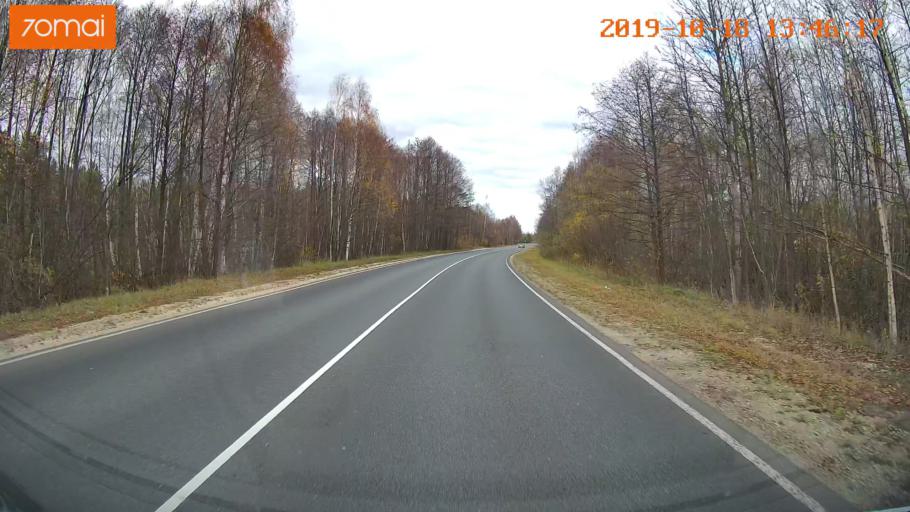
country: RU
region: Rjazan
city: Solotcha
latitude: 54.9589
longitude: 39.9394
